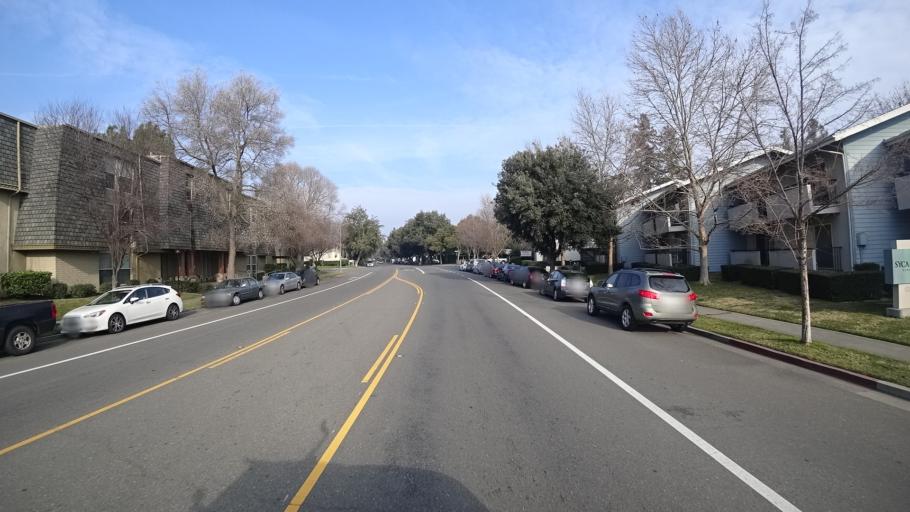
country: US
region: California
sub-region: Yolo County
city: Davis
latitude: 38.5479
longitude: -121.7620
